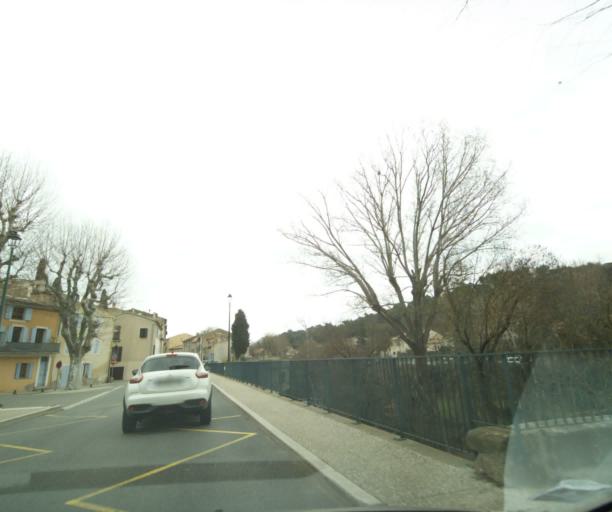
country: FR
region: Provence-Alpes-Cote d'Azur
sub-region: Departement des Bouches-du-Rhone
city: Jouques
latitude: 43.6370
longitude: 5.6344
